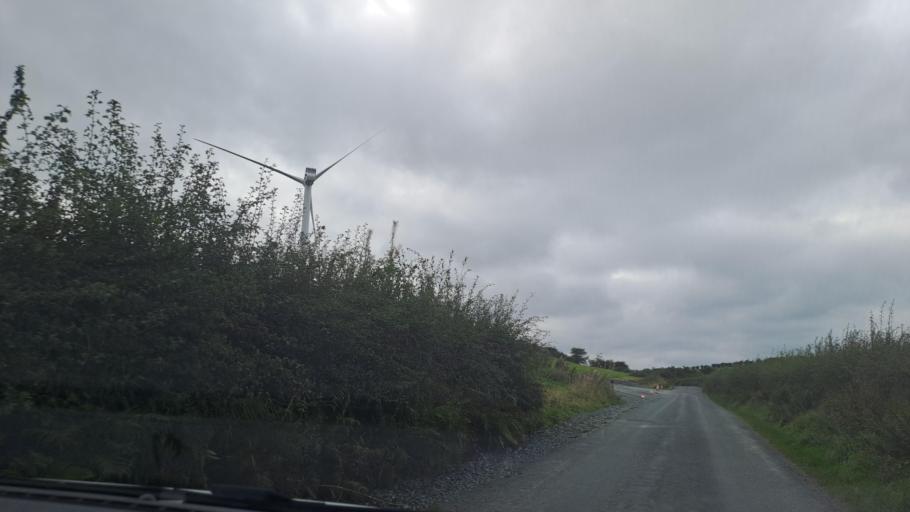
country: IE
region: Ulster
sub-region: An Cabhan
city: Kingscourt
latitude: 53.9561
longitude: -6.8824
